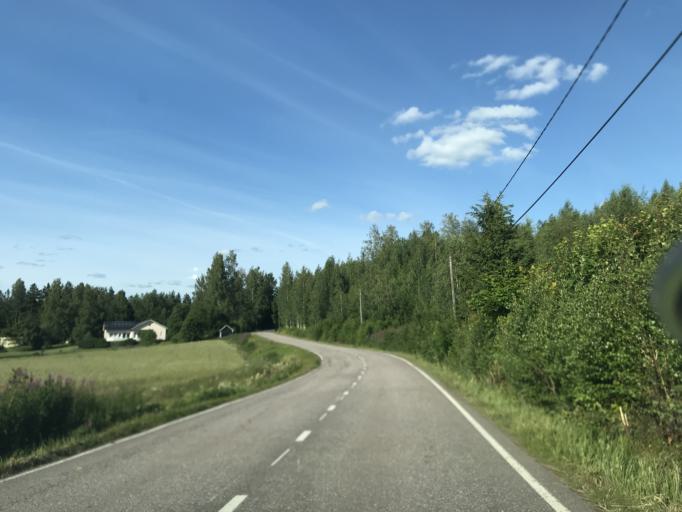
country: FI
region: Uusimaa
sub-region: Helsinki
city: Vihti
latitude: 60.4337
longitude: 24.5377
